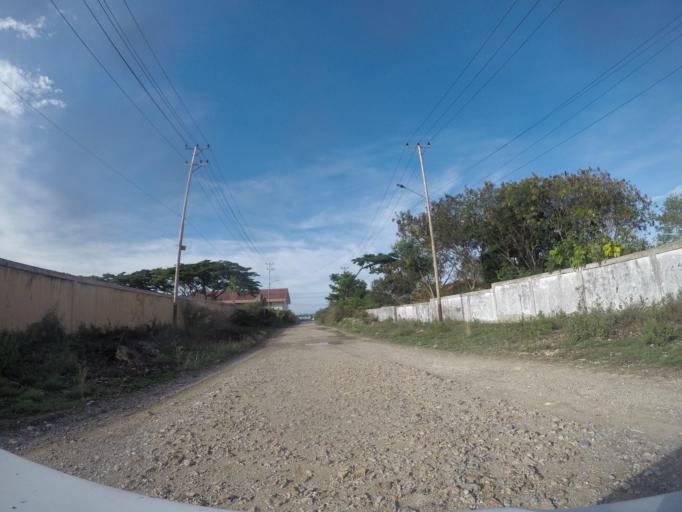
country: TL
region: Baucau
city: Baucau
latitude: -8.4850
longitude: 126.4546
